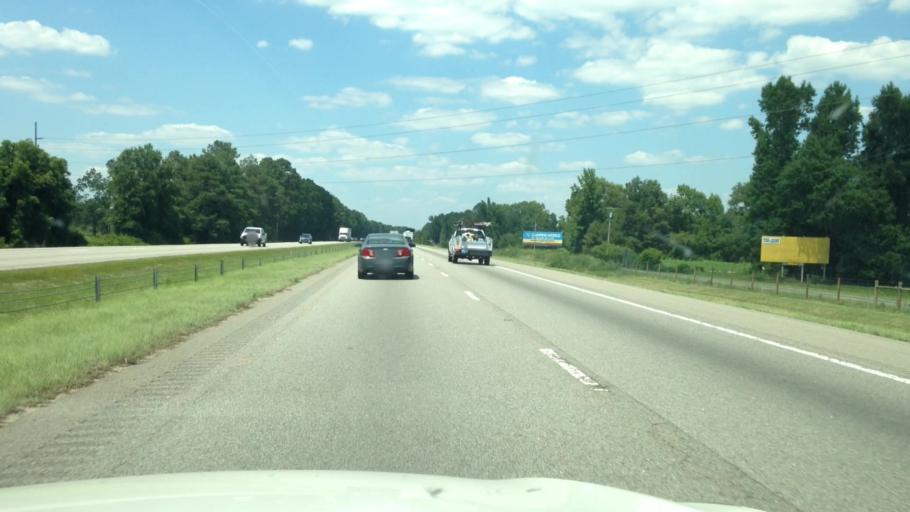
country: US
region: North Carolina
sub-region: Cumberland County
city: Hope Mills
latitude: 34.8930
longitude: -78.9595
